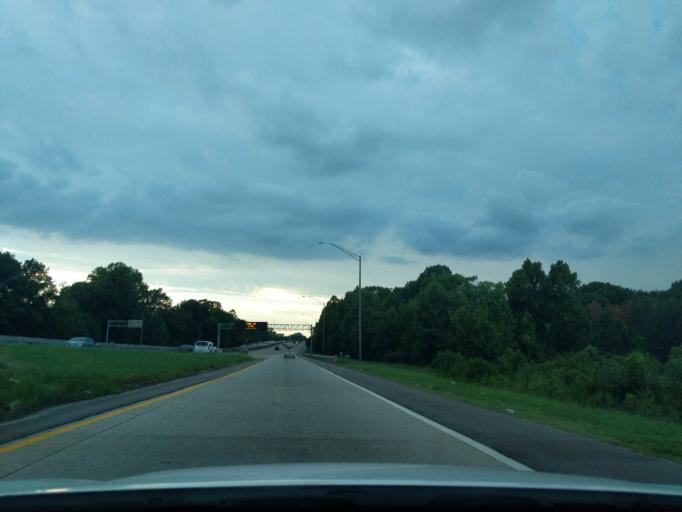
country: US
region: Tennessee
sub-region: Shelby County
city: Germantown
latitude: 35.0685
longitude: -89.8475
